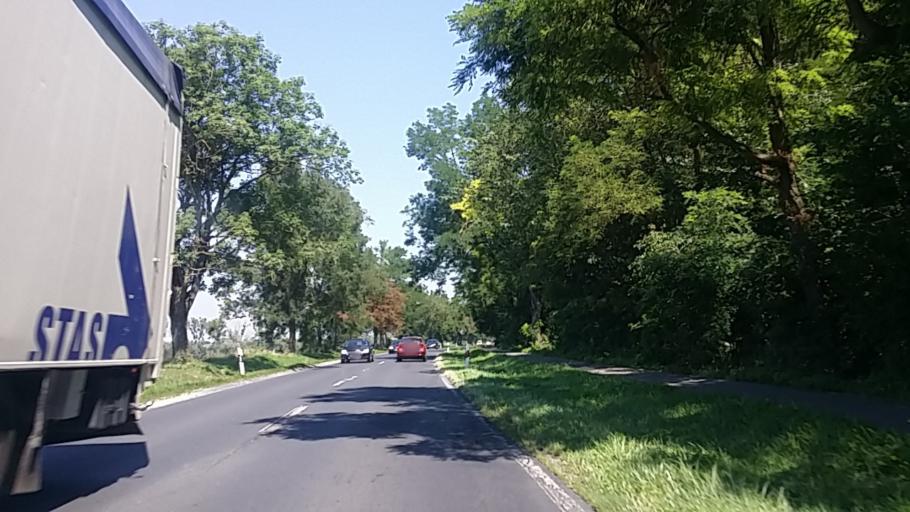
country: HU
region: Zala
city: Keszthely
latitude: 46.7158
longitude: 17.2427
